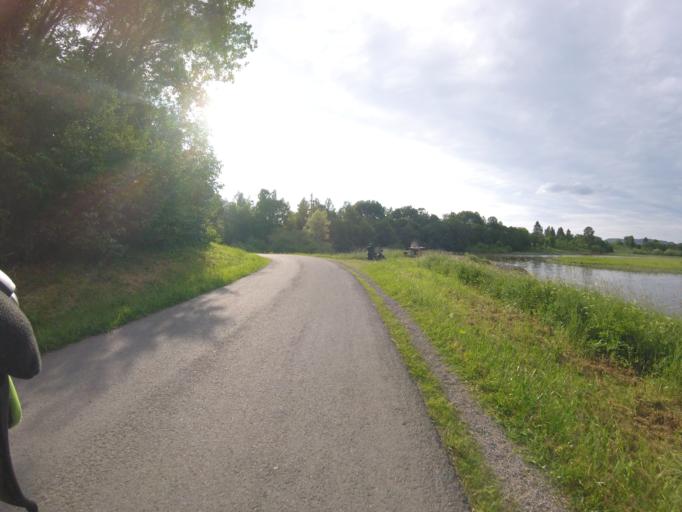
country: NO
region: Akershus
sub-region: Skedsmo
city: Lillestrom
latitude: 59.9688
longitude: 11.0146
